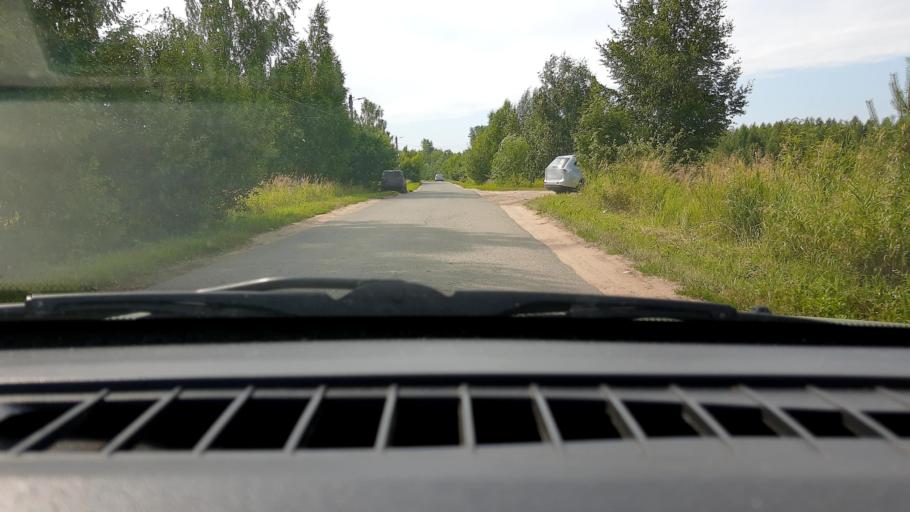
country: RU
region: Nizjnij Novgorod
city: Lukino
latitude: 56.4177
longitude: 43.7126
